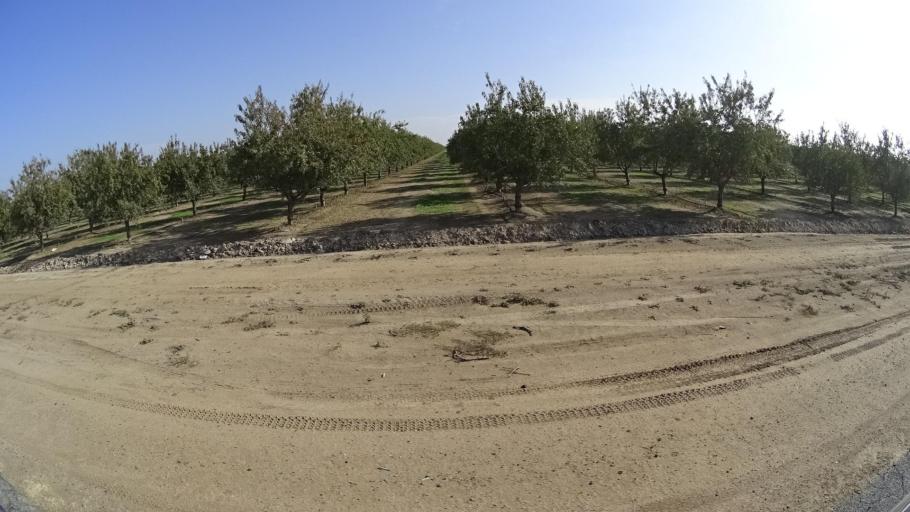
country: US
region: California
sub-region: Kern County
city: McFarland
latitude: 35.6858
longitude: -119.2048
